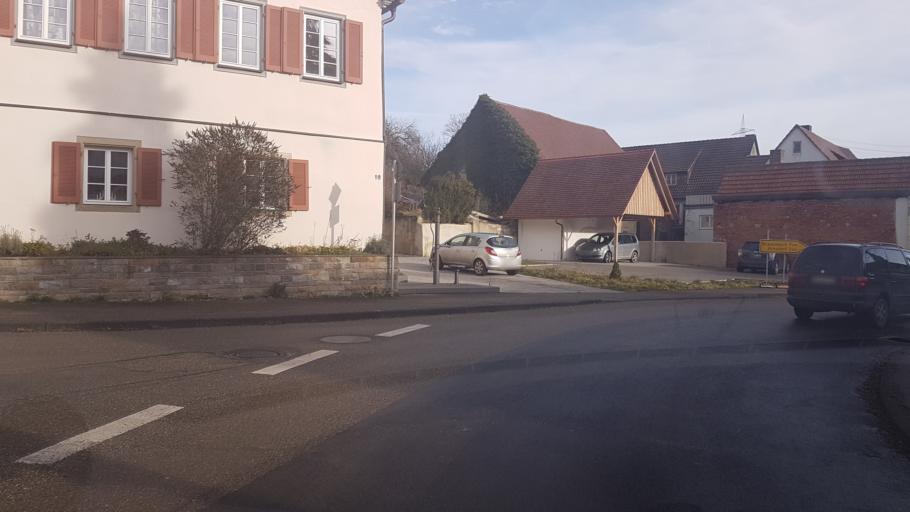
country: DE
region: Baden-Wuerttemberg
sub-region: Regierungsbezirk Stuttgart
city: Braunsbach
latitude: 49.2035
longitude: 9.7409
